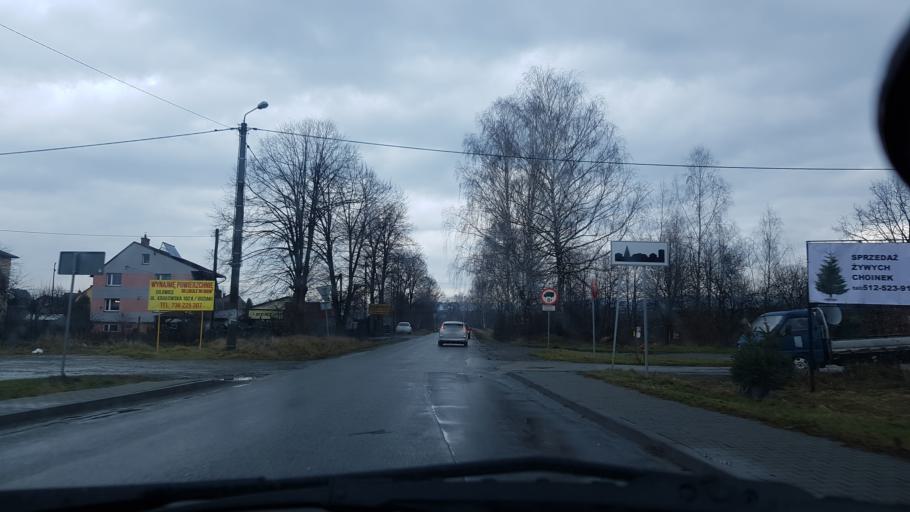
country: PL
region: Silesian Voivodeship
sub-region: Powiat zywiecki
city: Lekawica
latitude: 49.7112
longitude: 19.2377
